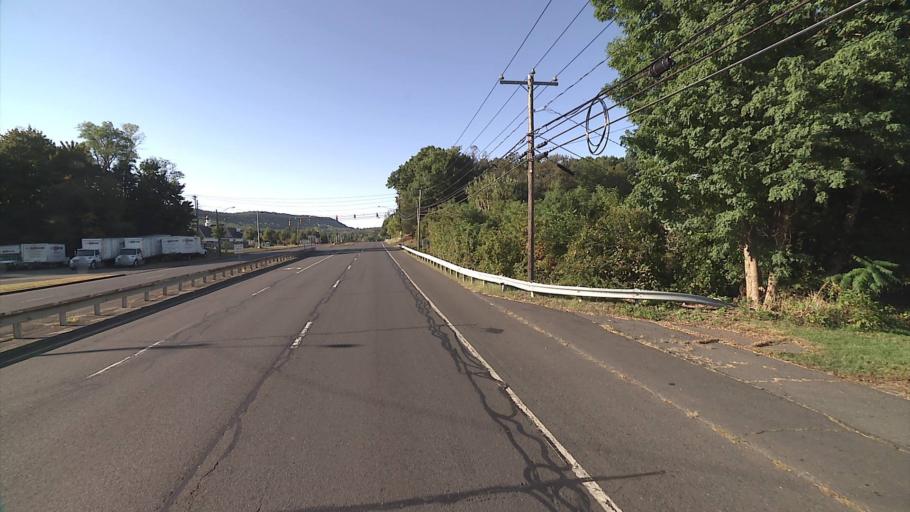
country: US
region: Connecticut
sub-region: Hartford County
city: Kensington
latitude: 41.6003
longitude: -72.7538
